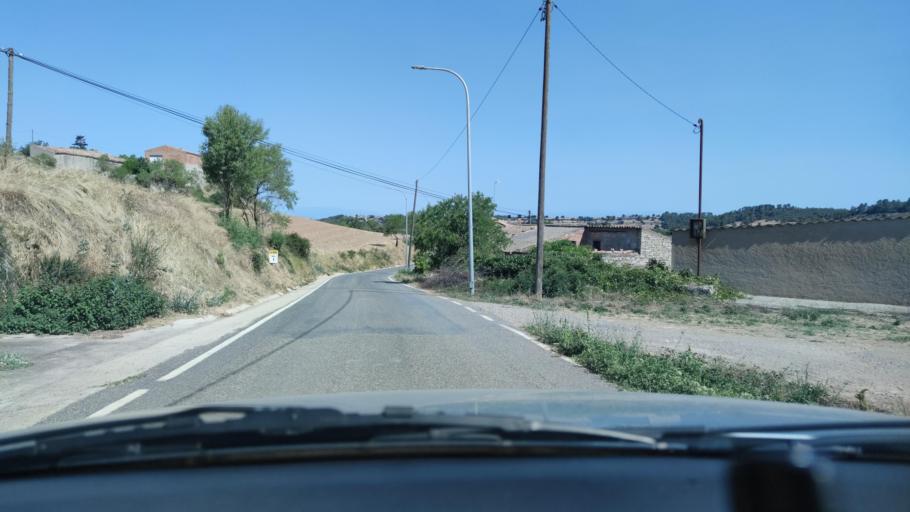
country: ES
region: Catalonia
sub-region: Provincia de Lleida
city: Sant Guim de Freixenet
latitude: 41.6619
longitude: 1.3680
